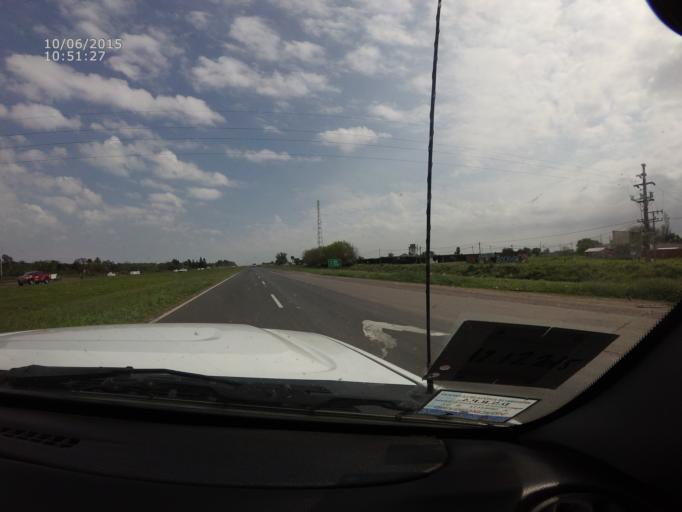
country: AR
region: Buenos Aires
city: San Nicolas de los Arroyos
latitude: -33.3633
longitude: -60.2561
